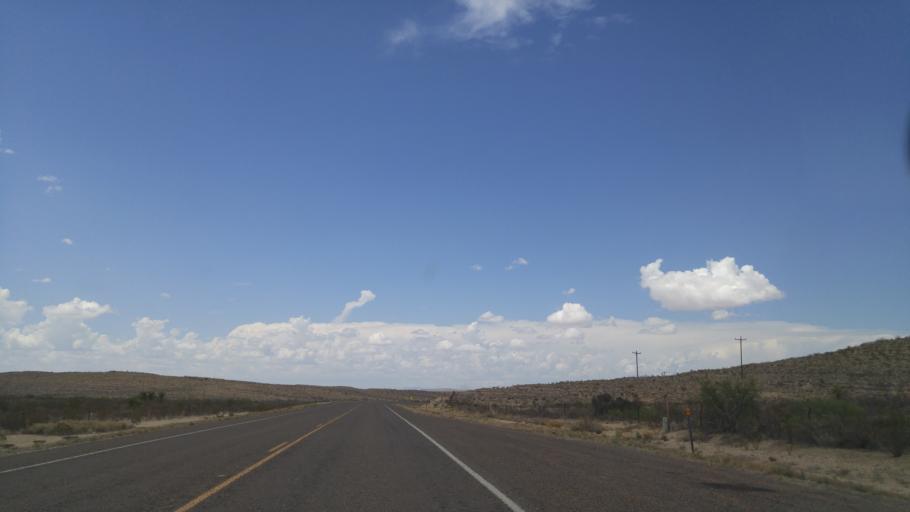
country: US
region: Texas
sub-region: Brewster County
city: Alpine
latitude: 29.5898
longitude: -103.5602
